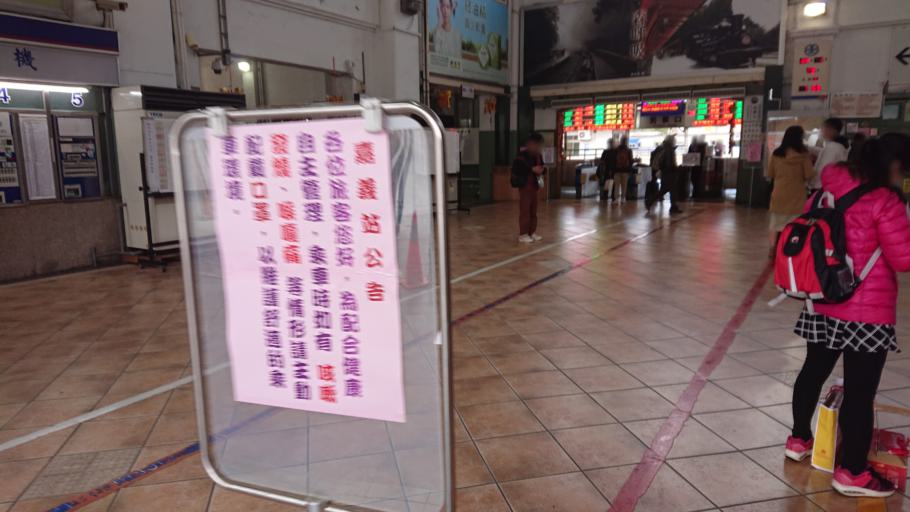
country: TW
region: Taiwan
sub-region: Chiayi
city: Jiayi Shi
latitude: 23.4791
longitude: 120.4413
